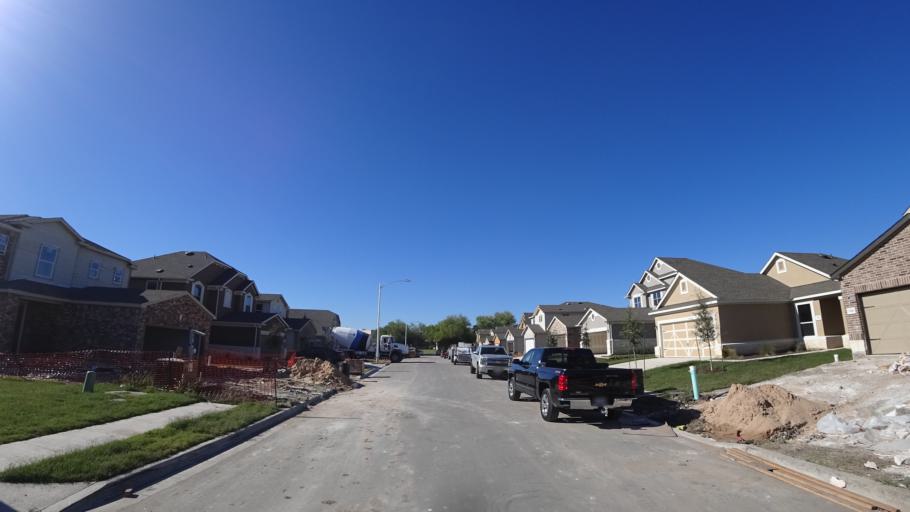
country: US
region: Texas
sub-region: Travis County
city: Hornsby Bend
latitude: 30.3160
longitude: -97.6554
